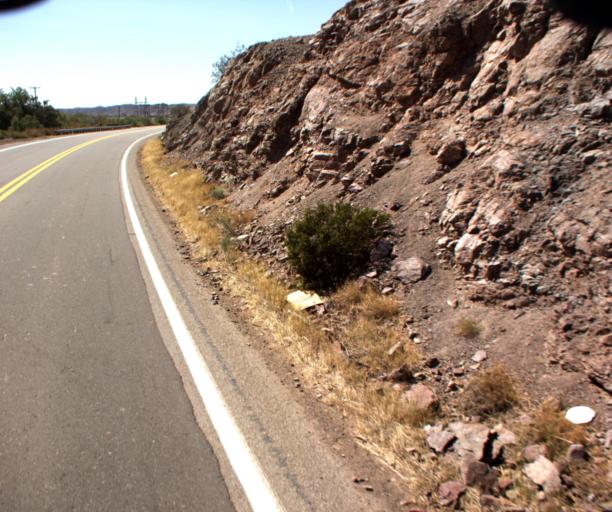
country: US
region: Arizona
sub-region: Yuma County
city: Fortuna Foothills
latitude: 32.7699
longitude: -114.3911
